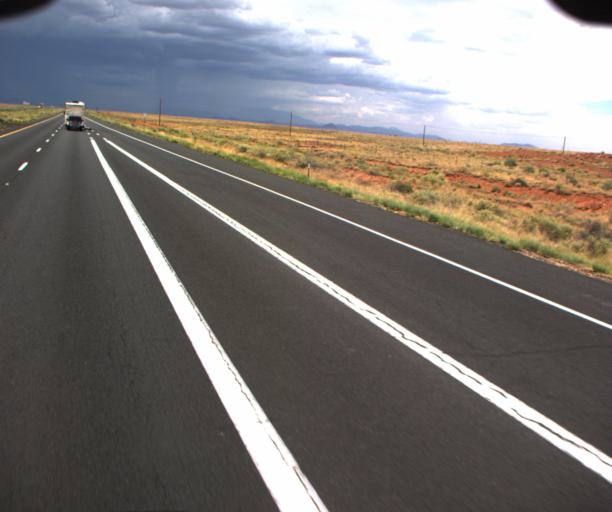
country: US
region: Arizona
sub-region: Coconino County
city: LeChee
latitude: 35.1109
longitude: -111.0357
